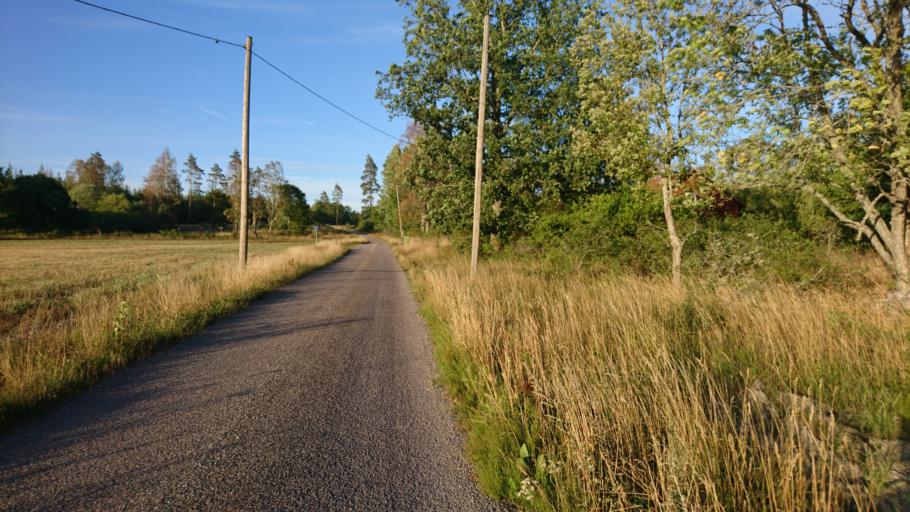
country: SE
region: Soedermanland
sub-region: Strangnas Kommun
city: Stallarholmen
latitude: 59.4004
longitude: 17.3089
